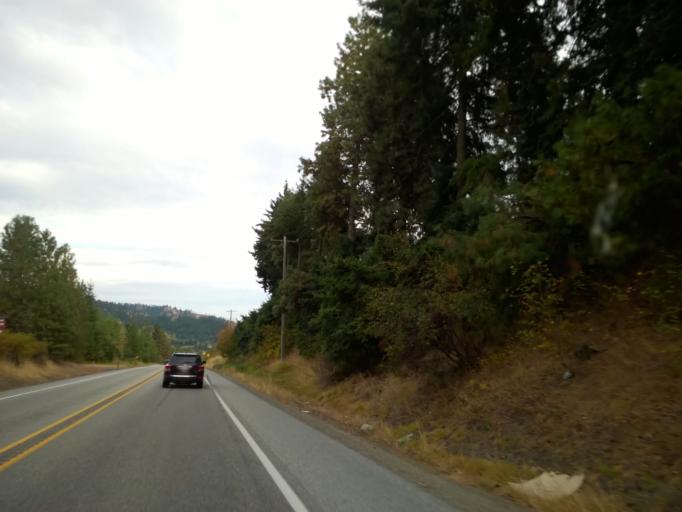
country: US
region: Washington
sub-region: Chelan County
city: Leavenworth
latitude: 47.5914
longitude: -120.6346
